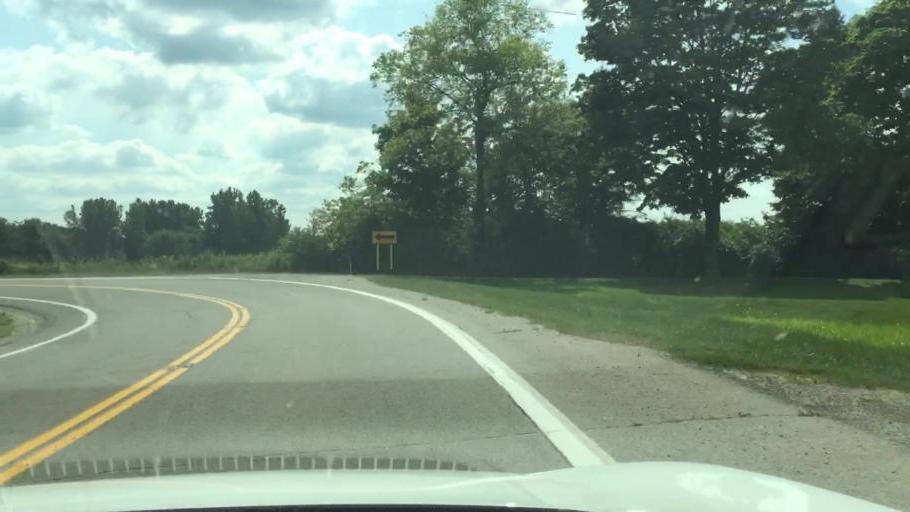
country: US
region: Ohio
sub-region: Champaign County
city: Mechanicsburg
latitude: 40.0868
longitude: -83.5557
